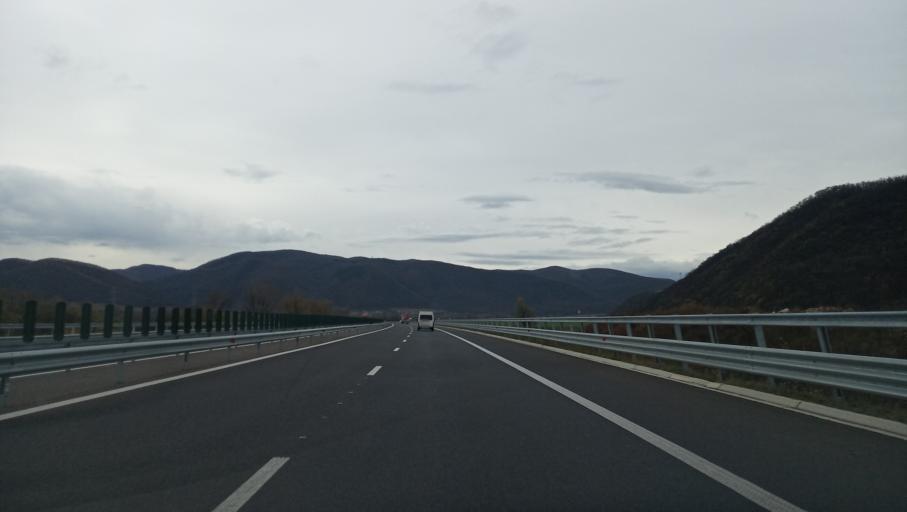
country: RO
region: Hunedoara
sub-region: Comuna Vetel
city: Vetel
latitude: 45.9183
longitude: 22.8170
